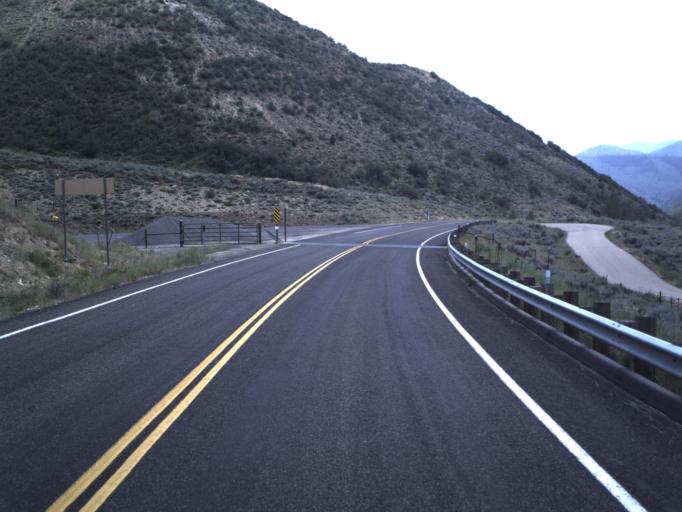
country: US
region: Utah
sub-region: Summit County
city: Francis
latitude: 40.4694
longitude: -110.9028
